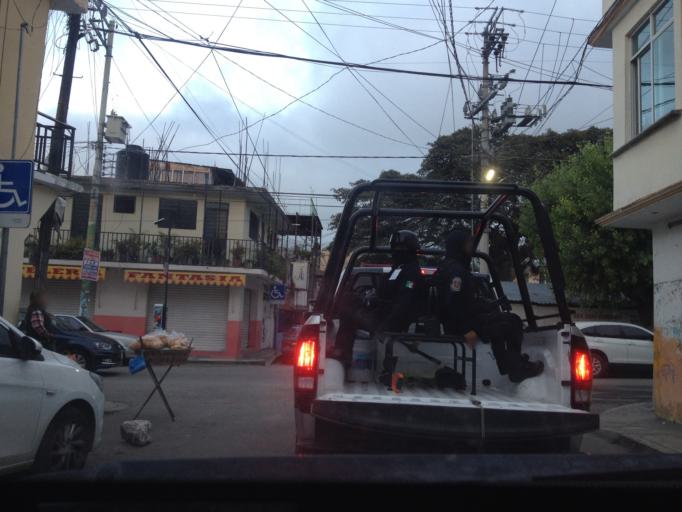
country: MX
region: Guerrero
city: Chilpancingo de los Bravos
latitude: 17.5478
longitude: -99.5007
